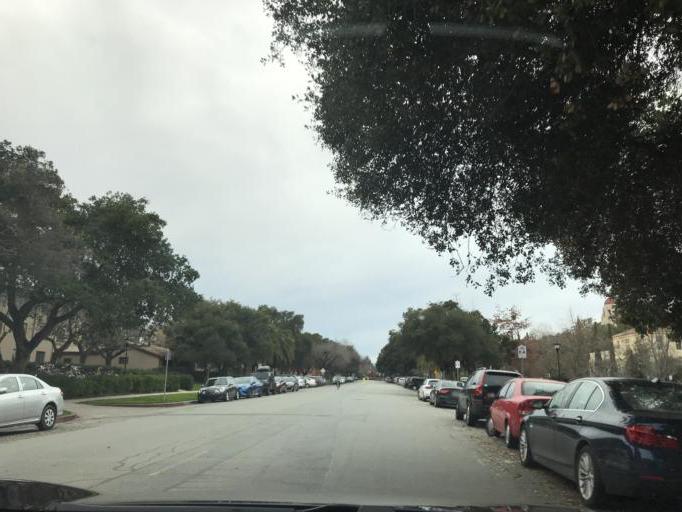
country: US
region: California
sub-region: Santa Clara County
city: Stanford
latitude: 37.4246
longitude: -122.1618
